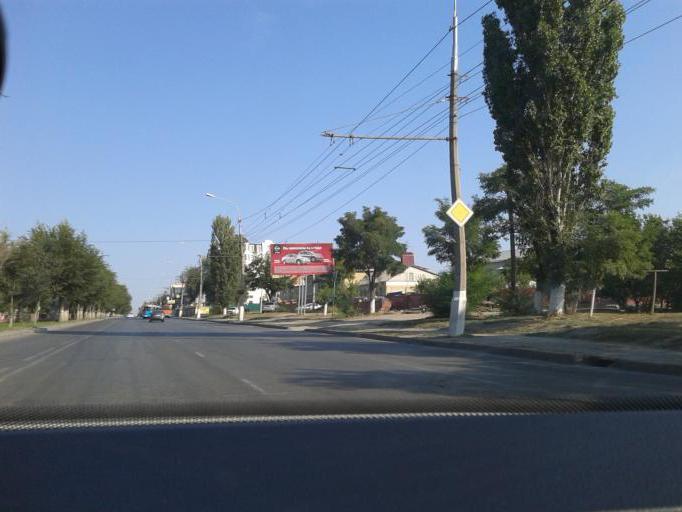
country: RU
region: Volgograd
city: Volgograd
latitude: 48.7248
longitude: 44.5014
